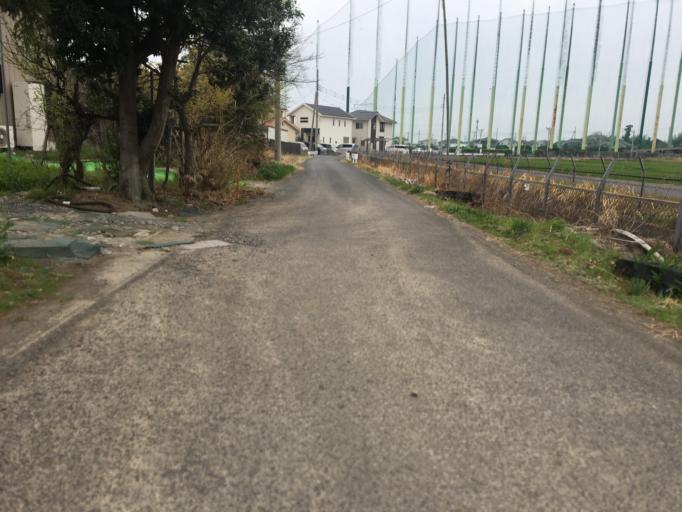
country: JP
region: Saitama
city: Kazo
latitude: 36.1073
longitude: 139.5966
